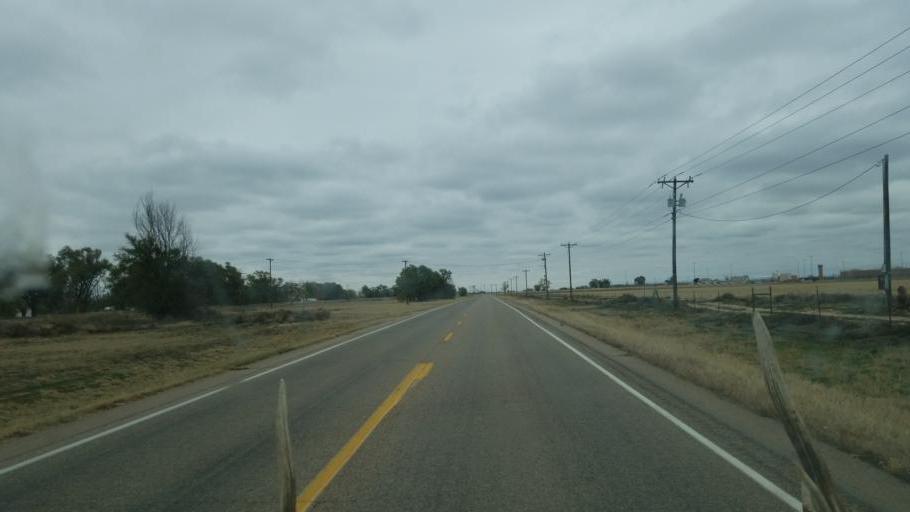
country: US
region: Colorado
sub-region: Crowley County
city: Ordway
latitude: 38.1926
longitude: -103.8535
